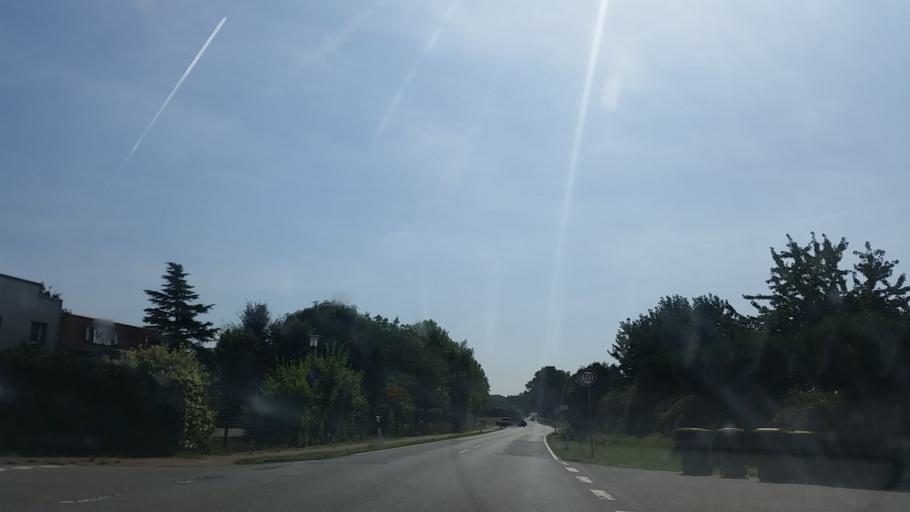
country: DE
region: Lower Saxony
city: Ankum
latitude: 52.5403
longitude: 7.8812
